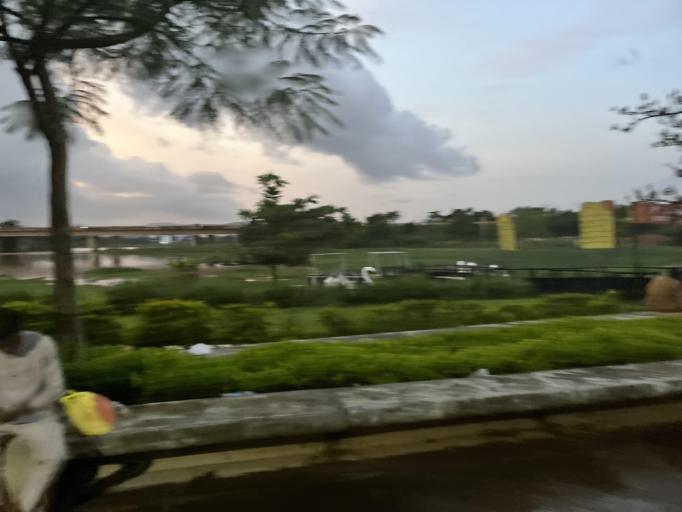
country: NG
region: Abuja Federal Capital Territory
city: Abuja
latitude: 9.0775
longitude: 7.4257
